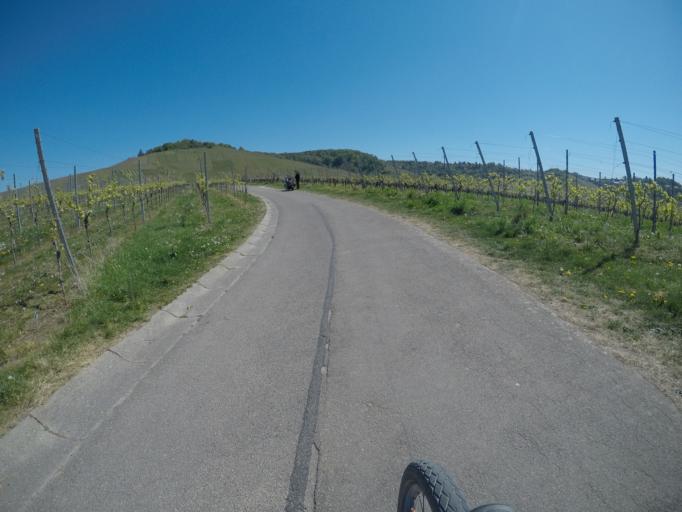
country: DE
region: Baden-Wuerttemberg
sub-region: Regierungsbezirk Stuttgart
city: Fellbach
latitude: 48.7951
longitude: 9.2696
